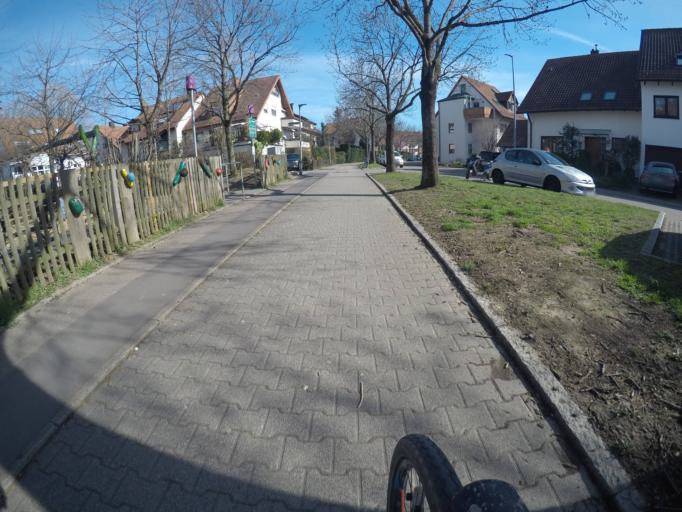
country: DE
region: Baden-Wuerttemberg
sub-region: Regierungsbezirk Stuttgart
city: Stuttgart Muehlhausen
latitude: 48.8401
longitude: 9.2591
